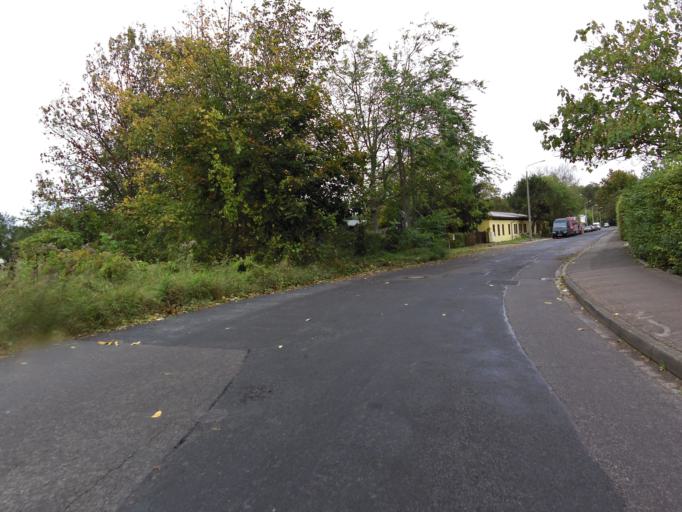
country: DE
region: Saxony
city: Markkleeberg
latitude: 51.2901
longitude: 12.3596
